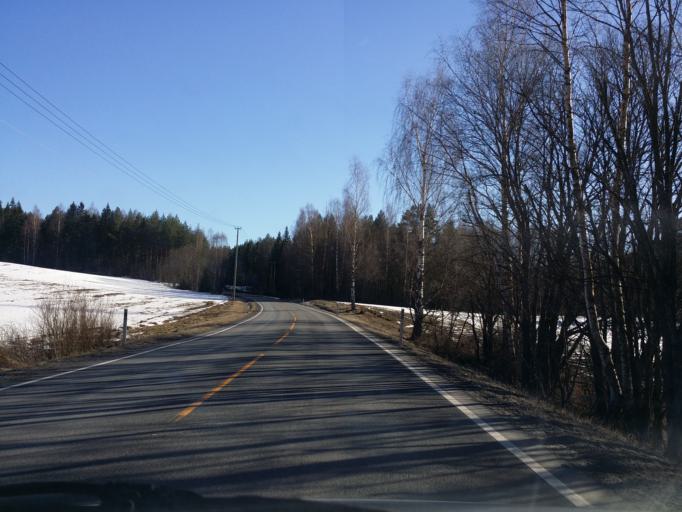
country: NO
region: Buskerud
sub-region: Ringerike
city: Honefoss
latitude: 60.3219
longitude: 10.1348
